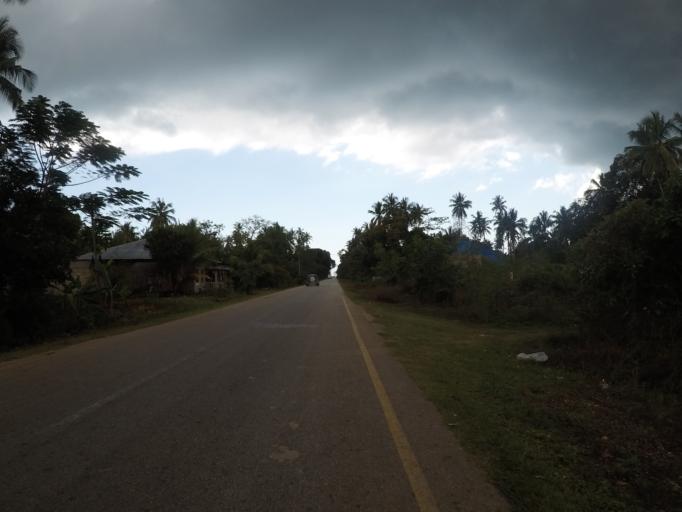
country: TZ
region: Zanzibar North
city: Mkokotoni
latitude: -5.9965
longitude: 39.1951
